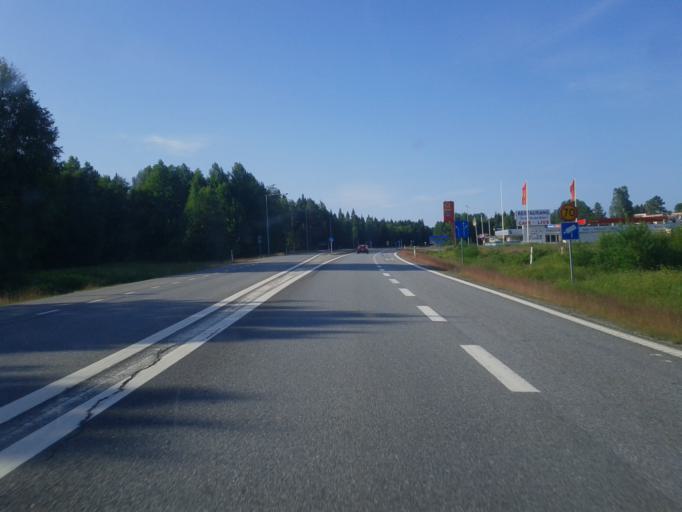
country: SE
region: Vaesterbotten
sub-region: Robertsfors Kommun
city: Robertsfors
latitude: 64.0593
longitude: 20.8477
